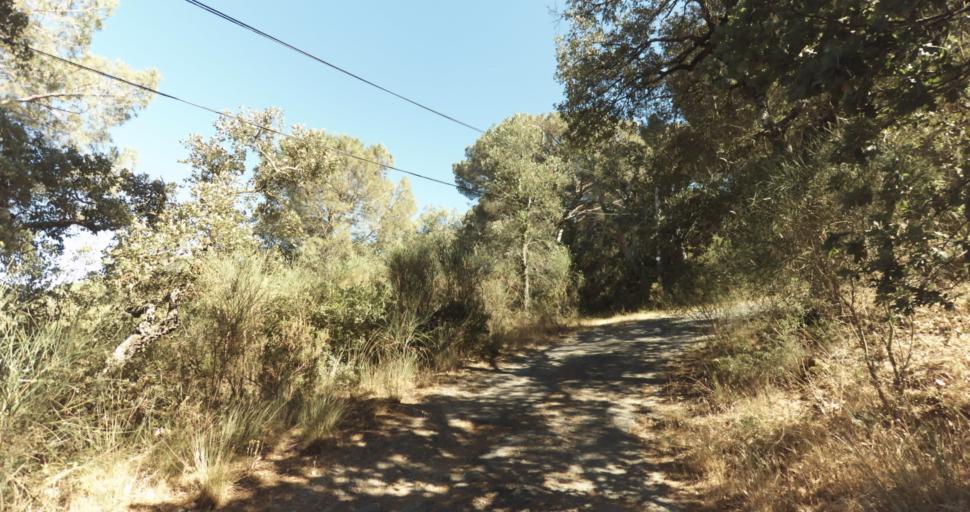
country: FR
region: Provence-Alpes-Cote d'Azur
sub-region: Departement du Var
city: Gassin
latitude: 43.2520
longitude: 6.5871
